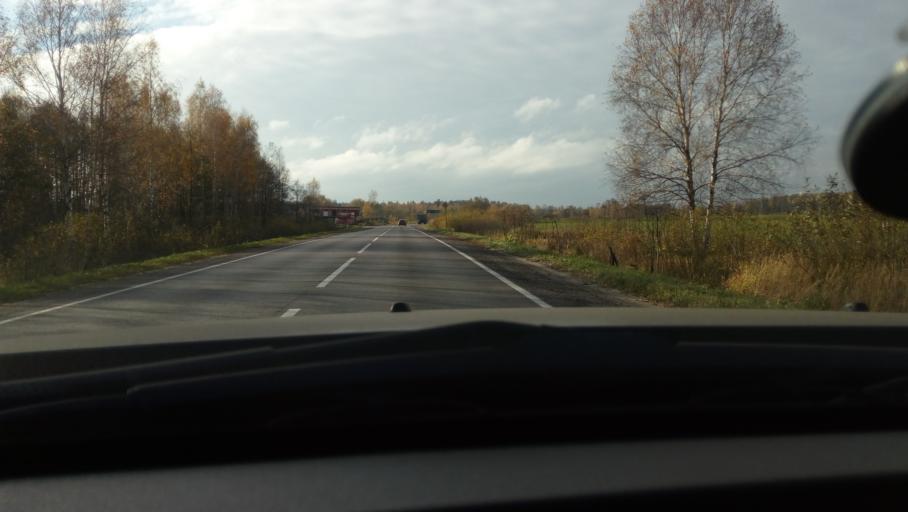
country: RU
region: Moskovskaya
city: Fryazevo
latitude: 55.7308
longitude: 38.4984
